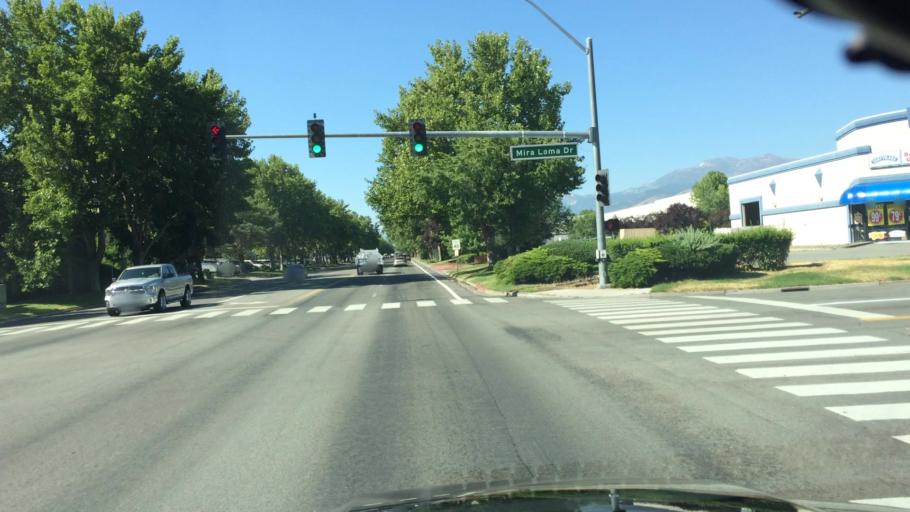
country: US
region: Nevada
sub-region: Washoe County
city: Sparks
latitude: 39.4876
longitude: -119.7602
